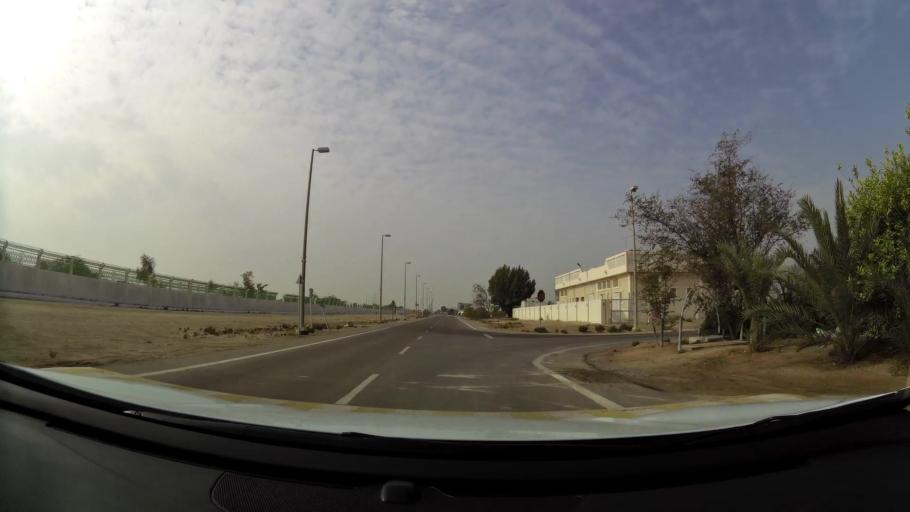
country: AE
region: Abu Dhabi
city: Abu Dhabi
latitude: 24.6661
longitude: 54.7741
